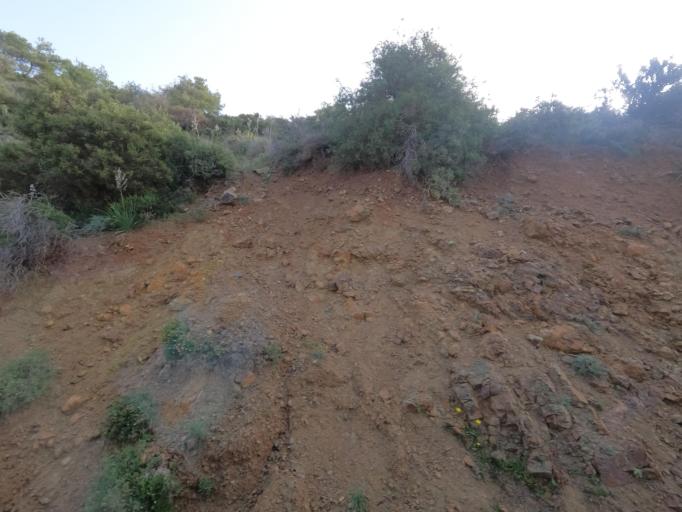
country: CY
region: Pafos
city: Polis
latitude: 35.0002
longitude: 32.3404
